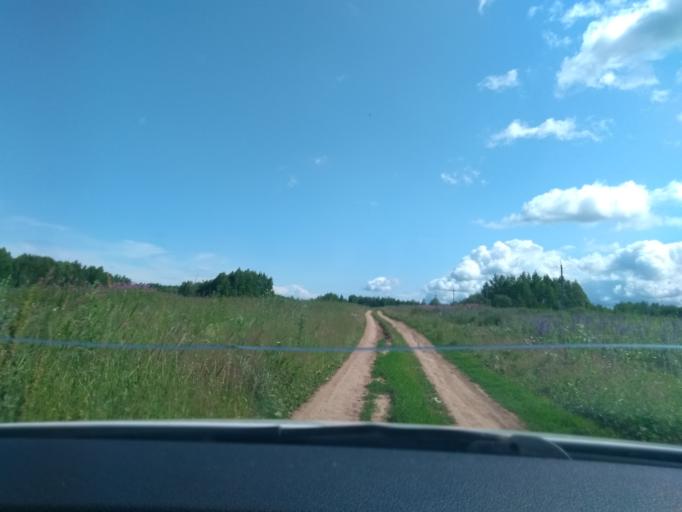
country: RU
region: Perm
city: Sylva
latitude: 57.8221
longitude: 56.7426
